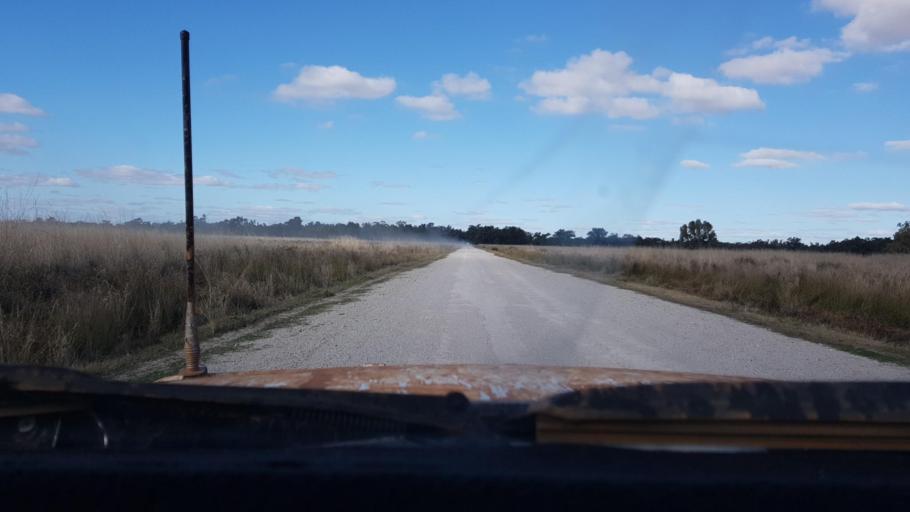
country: AU
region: New South Wales
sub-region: Lachlan
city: Condobolin
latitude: -33.1369
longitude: 147.2784
